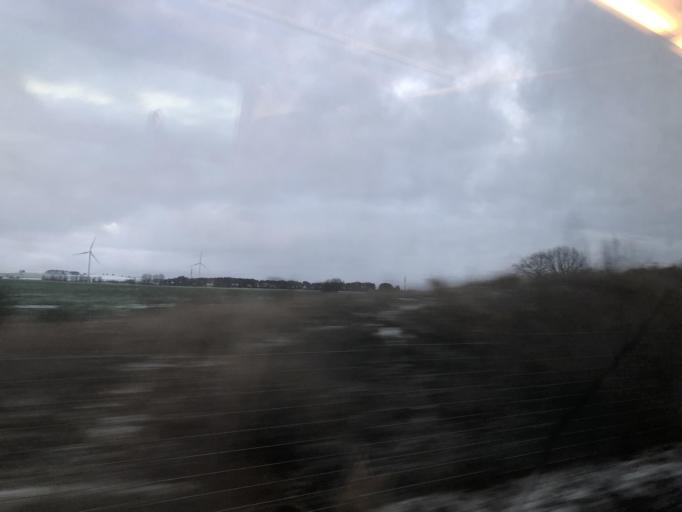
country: SE
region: Skane
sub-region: Landskrona
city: Asmundtorp
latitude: 55.8634
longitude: 12.8932
